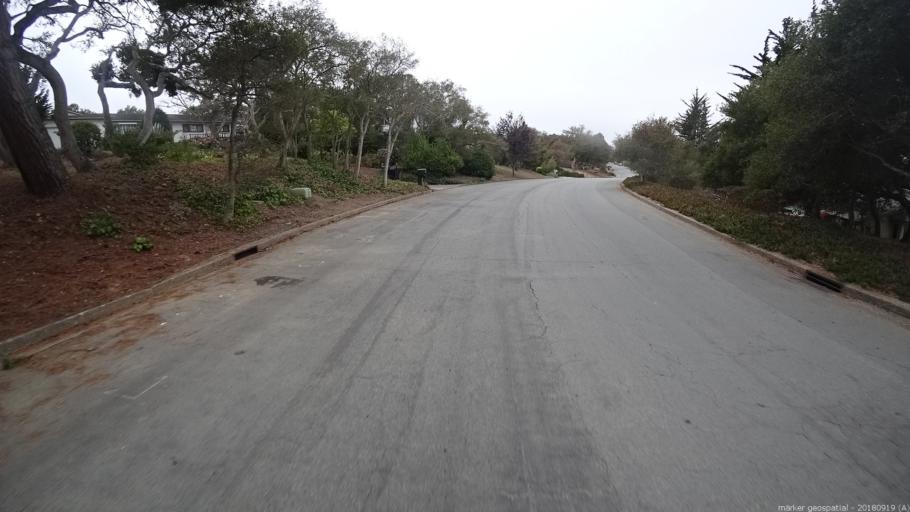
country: US
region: California
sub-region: Monterey County
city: Prunedale
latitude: 36.7819
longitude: -121.7074
